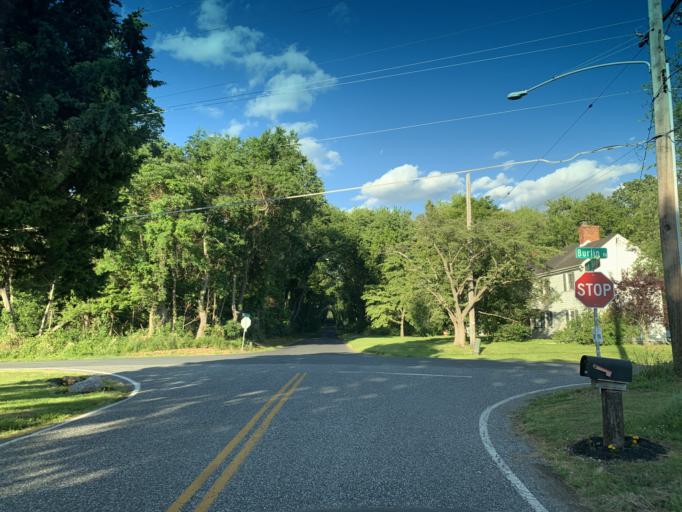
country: US
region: Maryland
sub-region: Cecil County
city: Perryville
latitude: 39.6261
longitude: -76.0981
